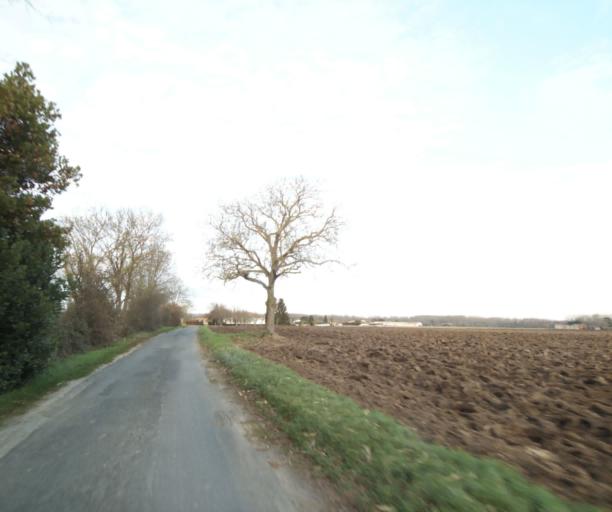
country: FR
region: Poitou-Charentes
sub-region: Departement de la Charente-Maritime
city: Les Gonds
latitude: 45.7083
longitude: -0.6123
